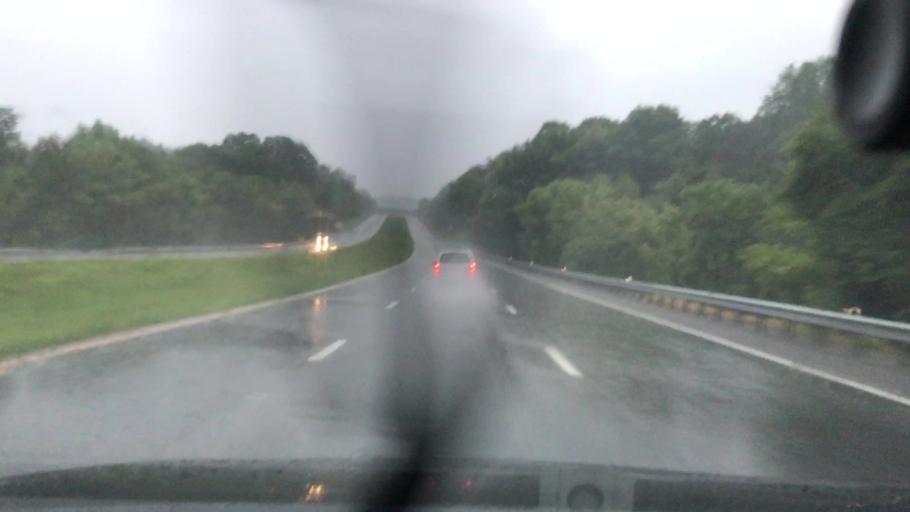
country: US
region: Virginia
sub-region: Giles County
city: Pearisburg
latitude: 37.3363
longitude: -80.7354
